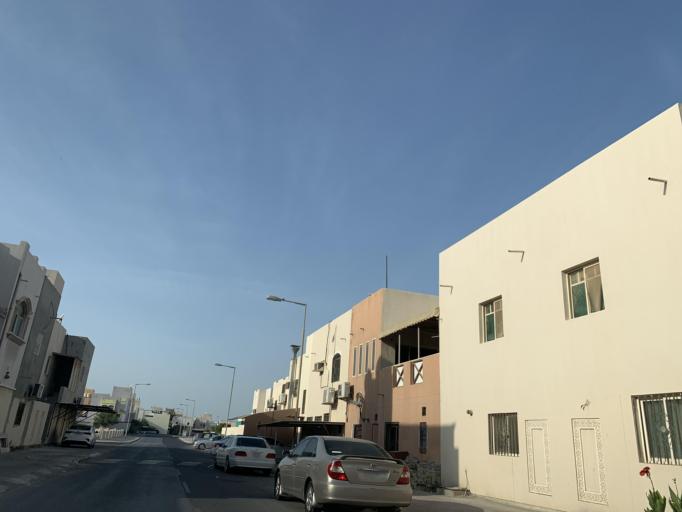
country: BH
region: Central Governorate
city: Madinat Hamad
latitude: 26.1231
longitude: 50.4868
